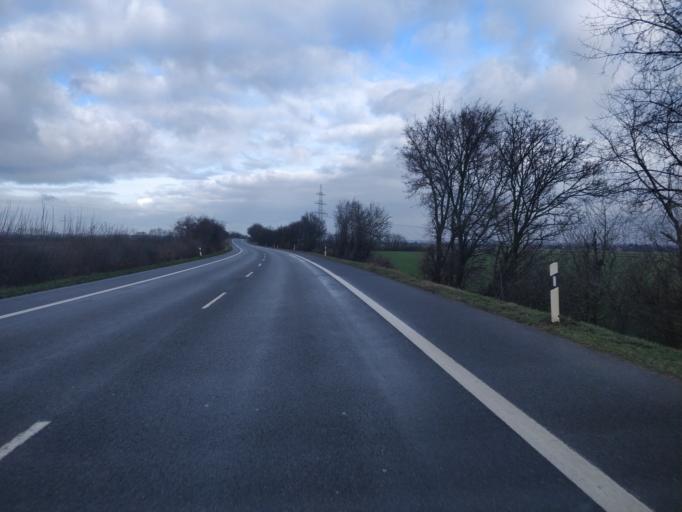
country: DE
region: North Rhine-Westphalia
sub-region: Regierungsbezirk Koln
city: Euskirchen
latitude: 50.6638
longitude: 6.8470
